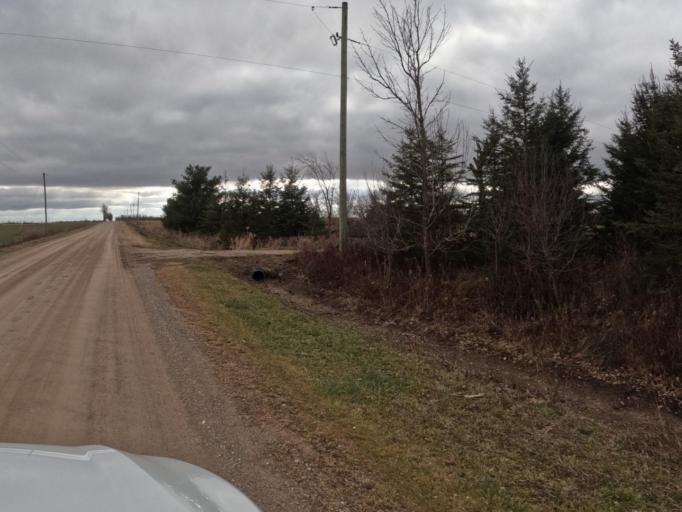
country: CA
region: Ontario
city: Shelburne
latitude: 43.8920
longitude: -80.3835
